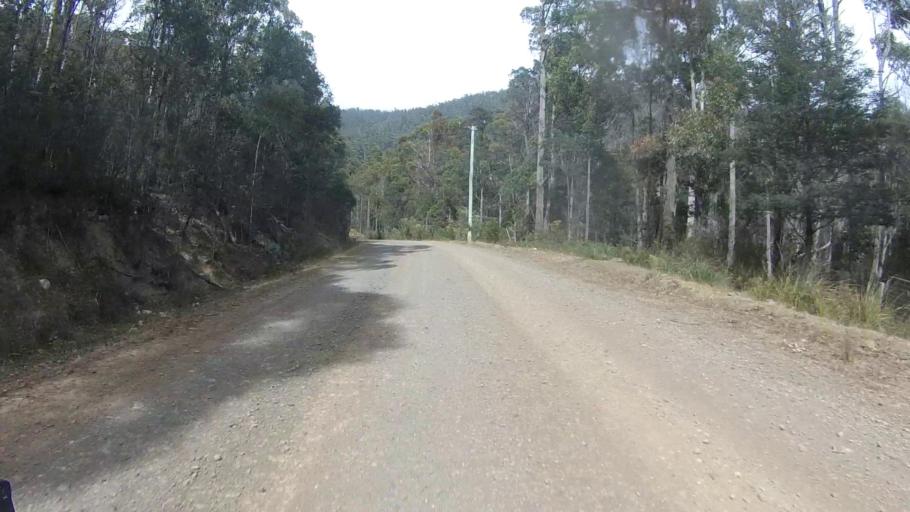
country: AU
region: Tasmania
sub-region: Sorell
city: Sorell
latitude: -42.6900
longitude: 147.8656
